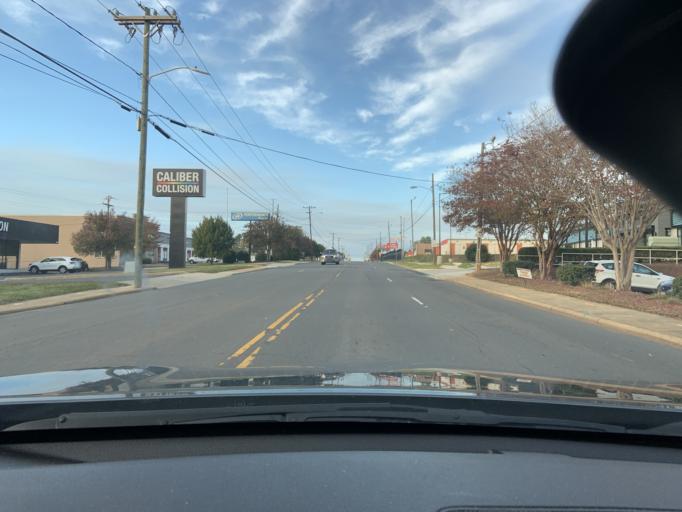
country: US
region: North Carolina
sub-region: Mecklenburg County
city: Charlotte
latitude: 35.1824
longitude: -80.8757
